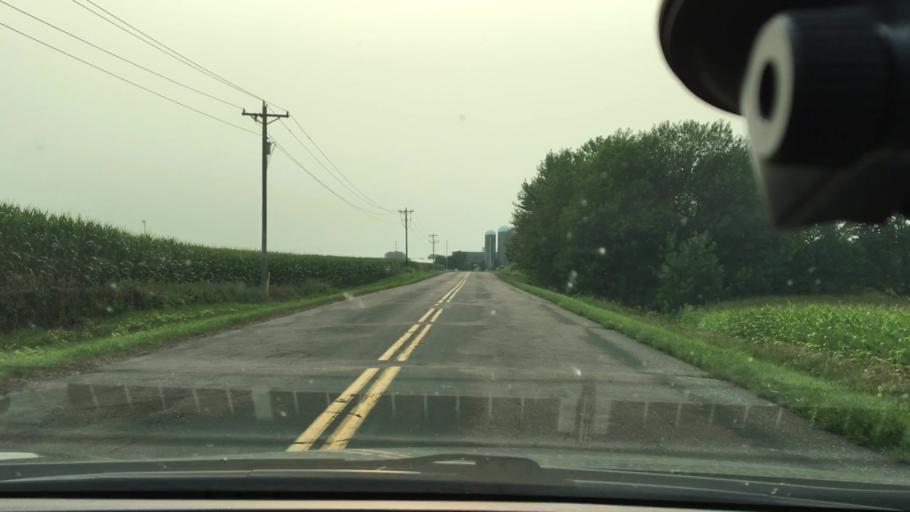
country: US
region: Minnesota
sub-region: Wright County
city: Albertville
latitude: 45.2665
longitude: -93.6799
